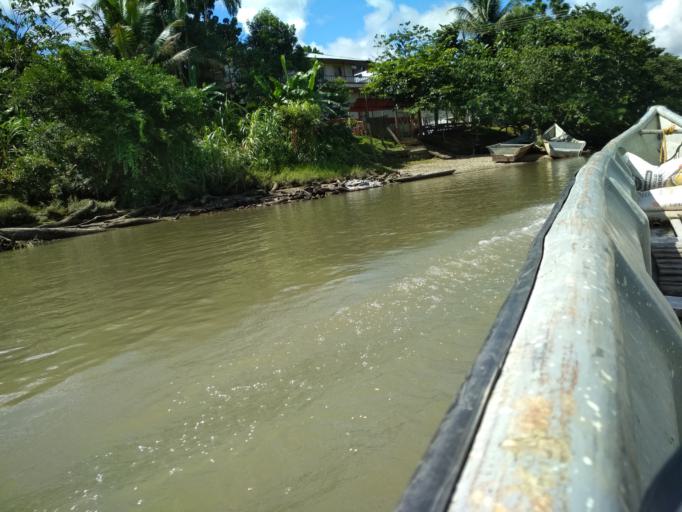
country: CO
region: Cauca
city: Timbiqui
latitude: 2.7544
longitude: -77.6630
